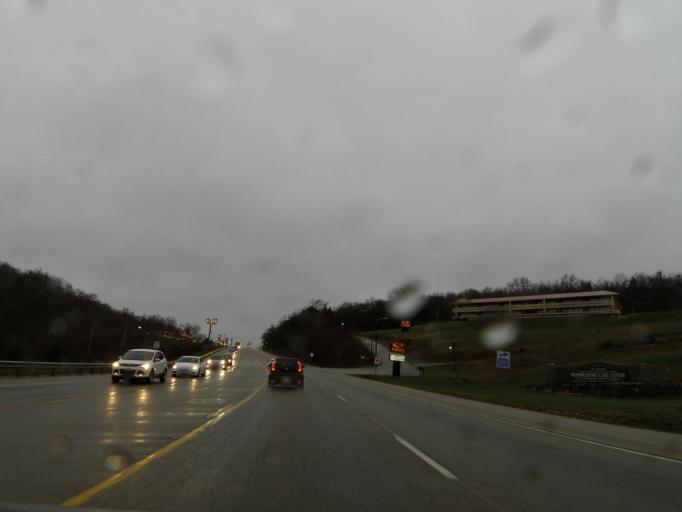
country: US
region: Kentucky
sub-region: Rockcastle County
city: Mount Vernon
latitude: 37.3741
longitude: -84.3330
